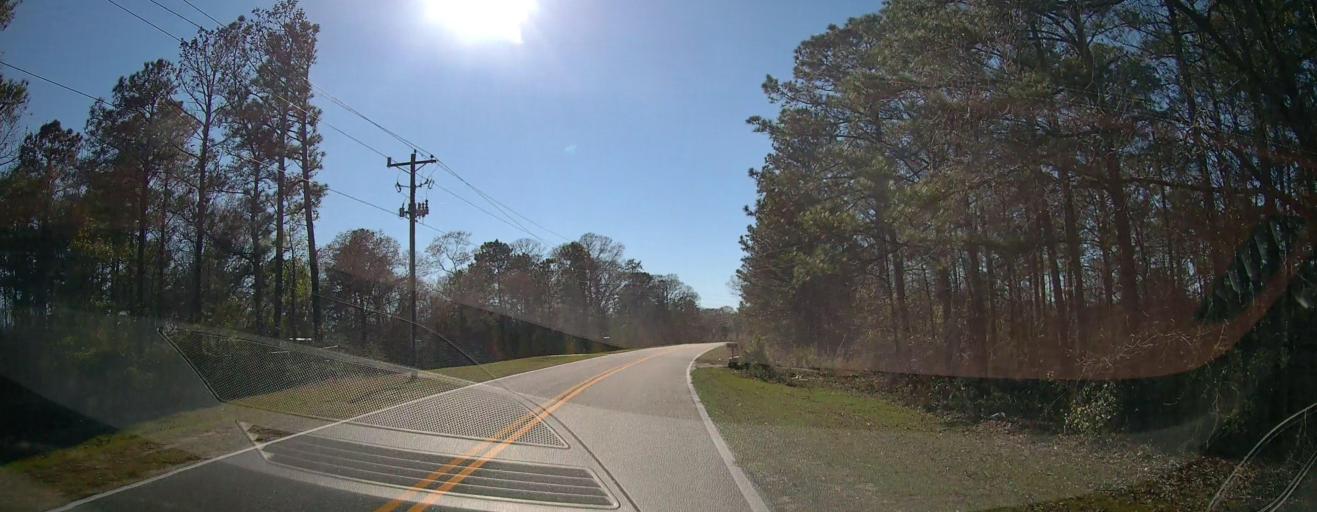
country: US
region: Georgia
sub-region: Peach County
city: Byron
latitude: 32.6914
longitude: -83.7943
